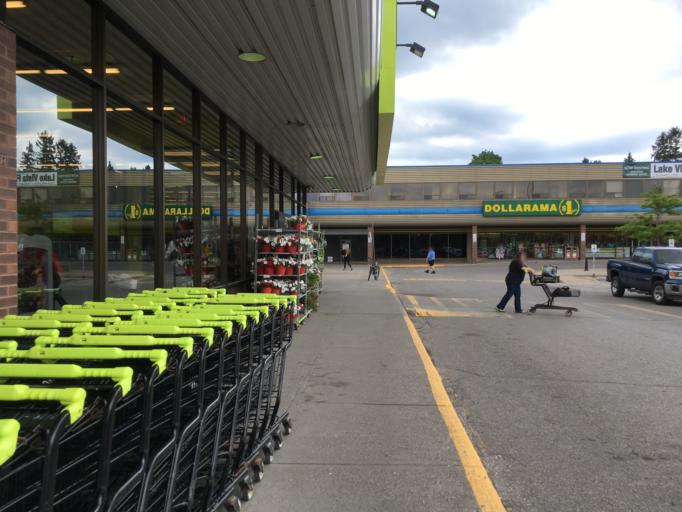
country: CA
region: Ontario
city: Oshawa
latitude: 43.8699
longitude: -78.8495
